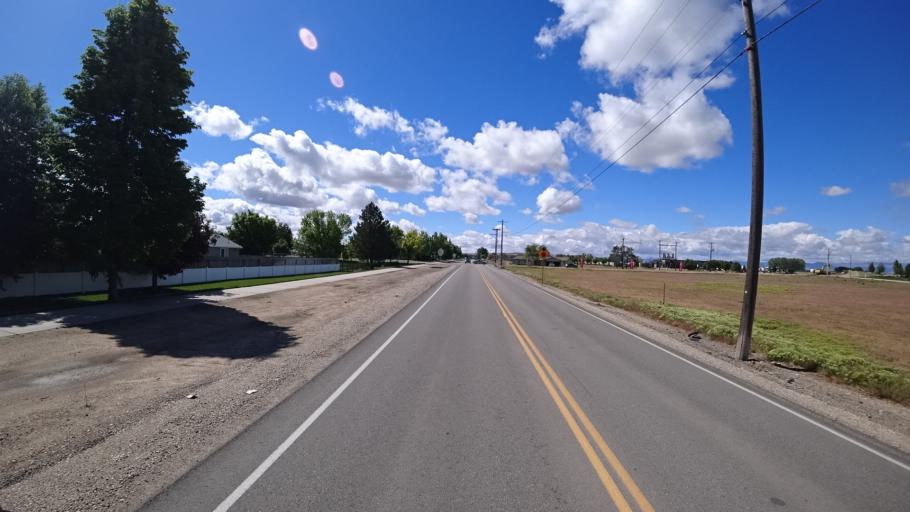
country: US
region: Idaho
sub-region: Ada County
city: Kuna
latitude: 43.5039
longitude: -116.4337
